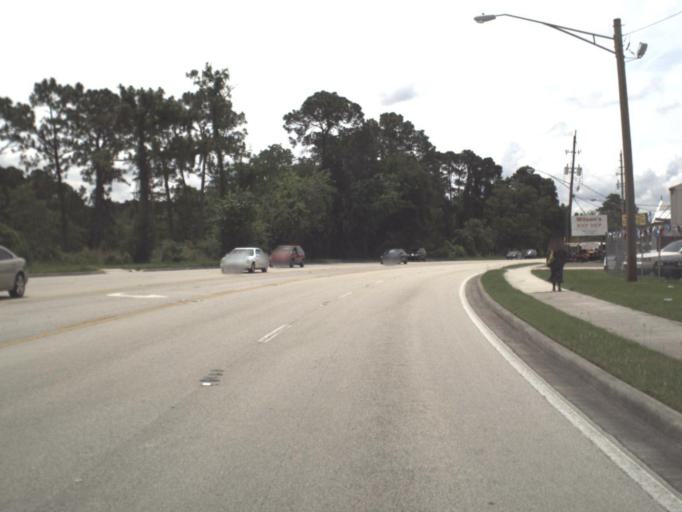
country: US
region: Florida
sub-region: Duval County
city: Jacksonville
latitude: 30.4376
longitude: -81.6761
